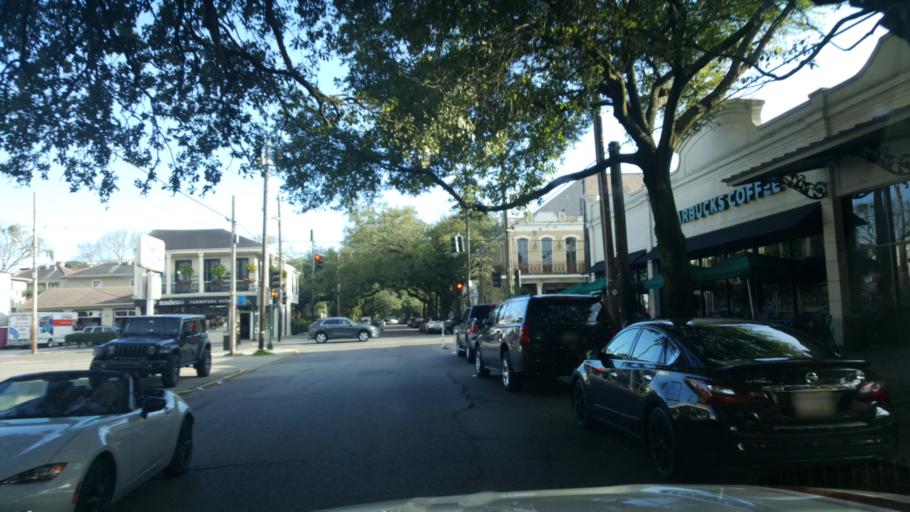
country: US
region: Louisiana
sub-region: Jefferson Parish
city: Harvey
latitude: 29.9267
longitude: -90.0829
